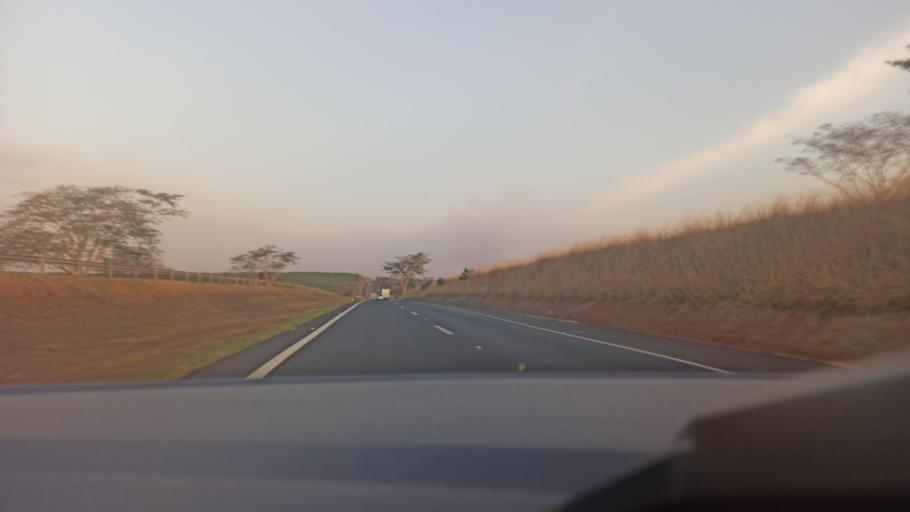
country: BR
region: Sao Paulo
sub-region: Taquaritinga
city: Taquaritinga
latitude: -21.4437
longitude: -48.6449
